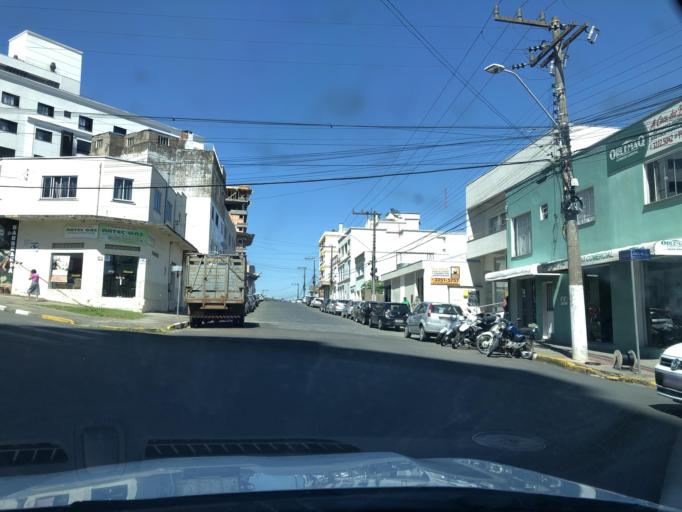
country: BR
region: Santa Catarina
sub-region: Lages
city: Lages
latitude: -27.8145
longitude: -50.3307
